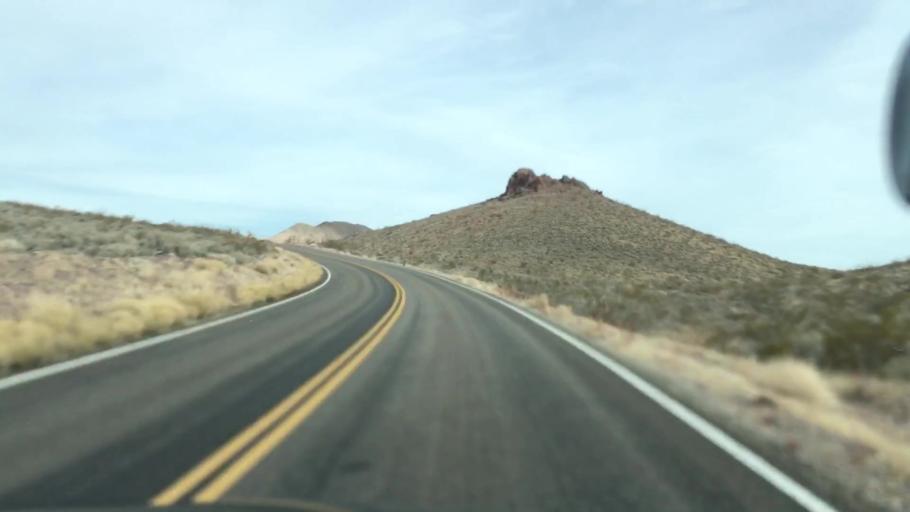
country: US
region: Nevada
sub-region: Nye County
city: Beatty
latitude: 36.7846
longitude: -116.9310
